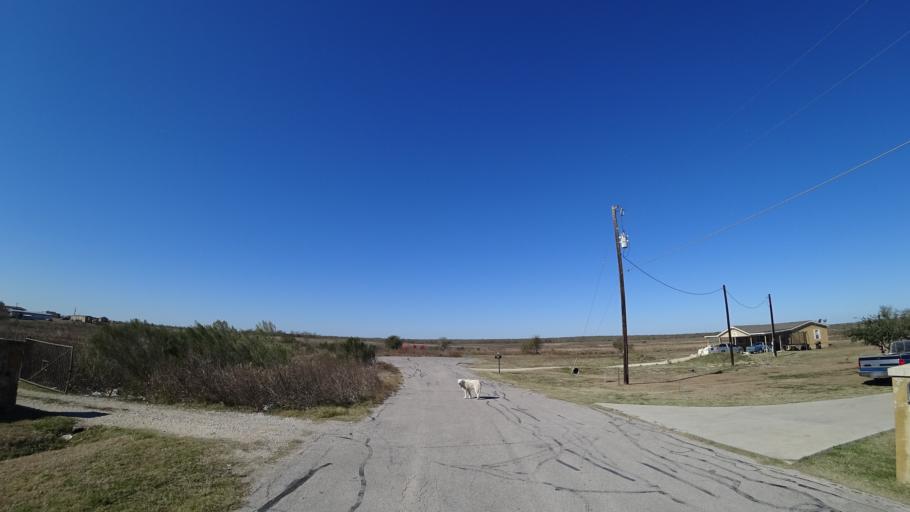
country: US
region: Texas
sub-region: Travis County
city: Garfield
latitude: 30.1085
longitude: -97.6001
